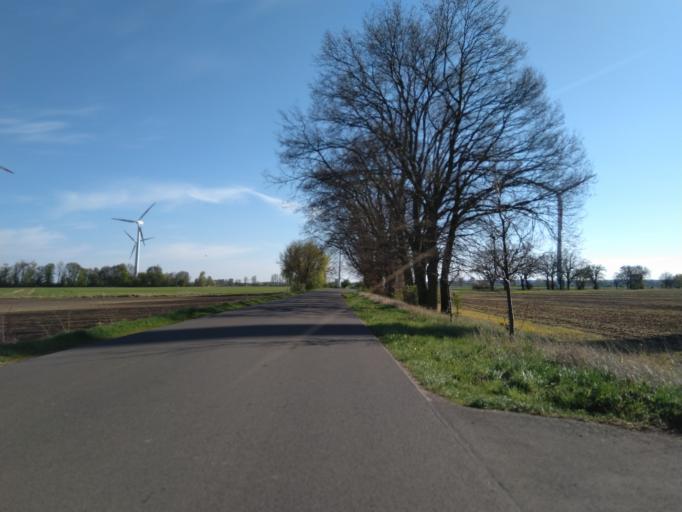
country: DE
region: Brandenburg
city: Bliesdorf
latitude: 52.7033
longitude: 14.1844
